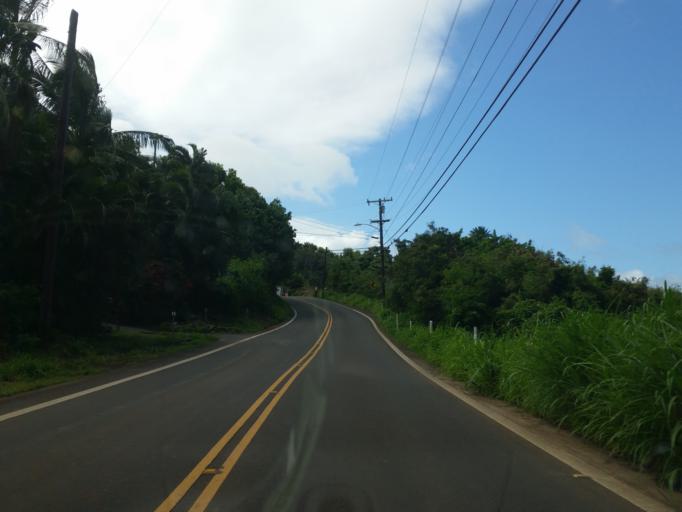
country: US
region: Hawaii
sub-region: Maui County
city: Waihee-Waiehu
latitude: 20.9457
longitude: -156.5167
